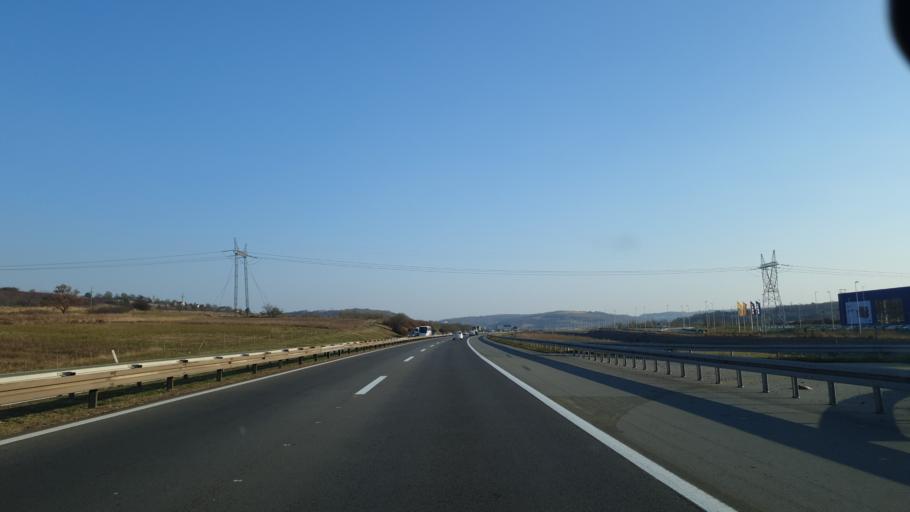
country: RS
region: Central Serbia
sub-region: Belgrade
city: Zvezdara
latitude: 44.7129
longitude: 20.5631
